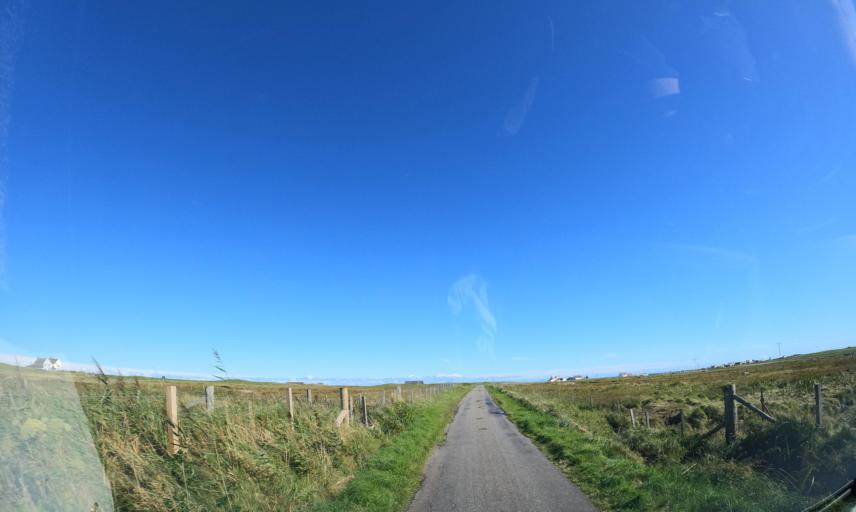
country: GB
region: Scotland
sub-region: Eilean Siar
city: Barra
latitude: 56.4732
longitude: -6.9061
